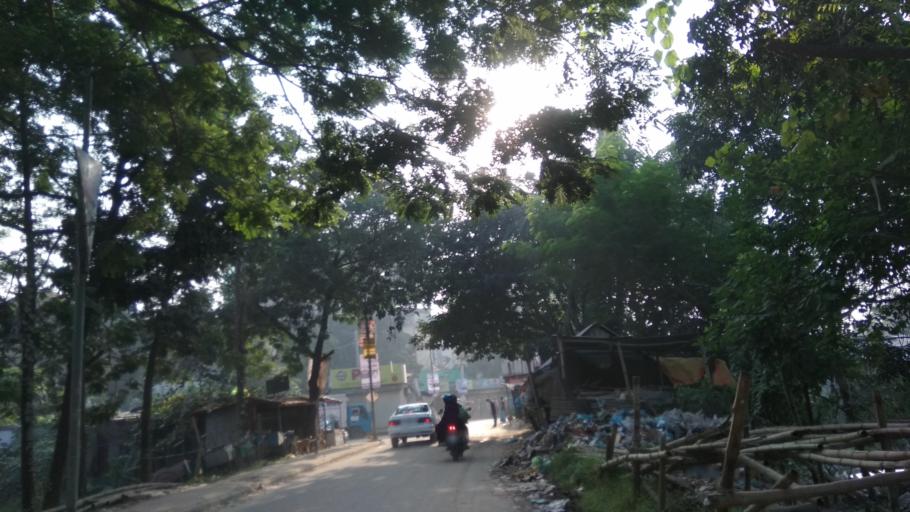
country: BD
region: Dhaka
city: Tungi
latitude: 23.8463
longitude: 90.4193
